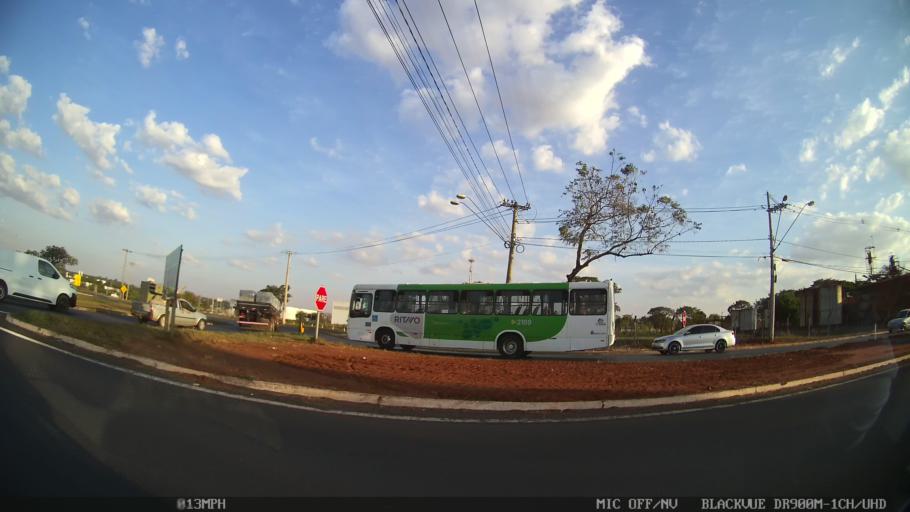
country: BR
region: Sao Paulo
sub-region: Ribeirao Preto
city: Ribeirao Preto
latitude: -21.1491
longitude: -47.7591
